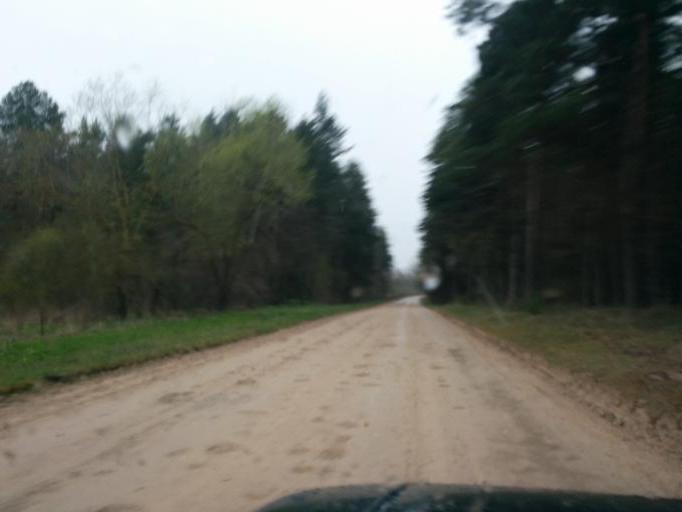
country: LV
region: Lecava
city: Iecava
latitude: 56.6177
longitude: 24.1760
